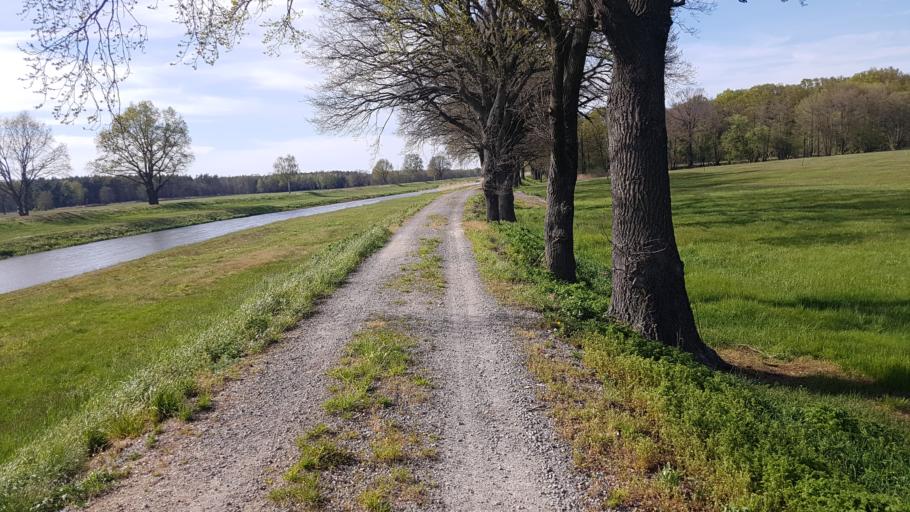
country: DE
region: Brandenburg
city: Falkenberg
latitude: 51.6202
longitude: 13.2895
